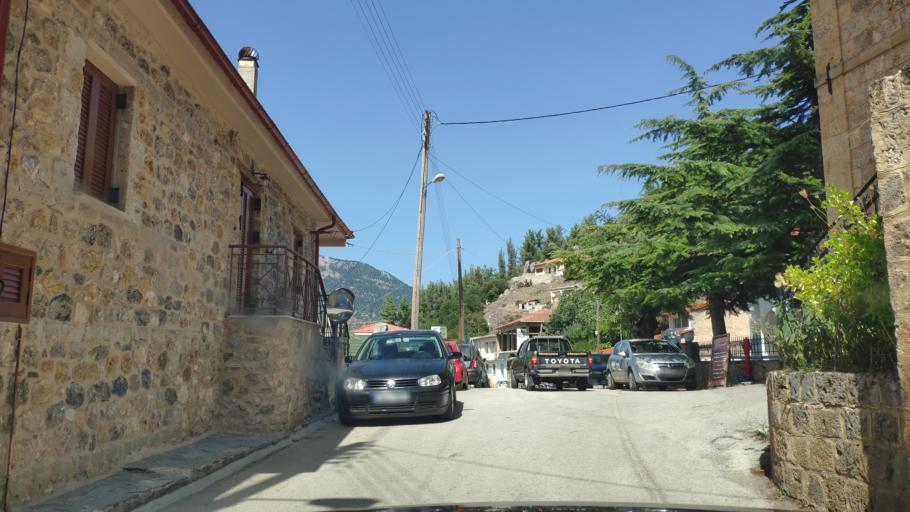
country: GR
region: West Greece
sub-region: Nomos Achaias
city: Aiyira
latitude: 37.9336
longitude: 22.3407
